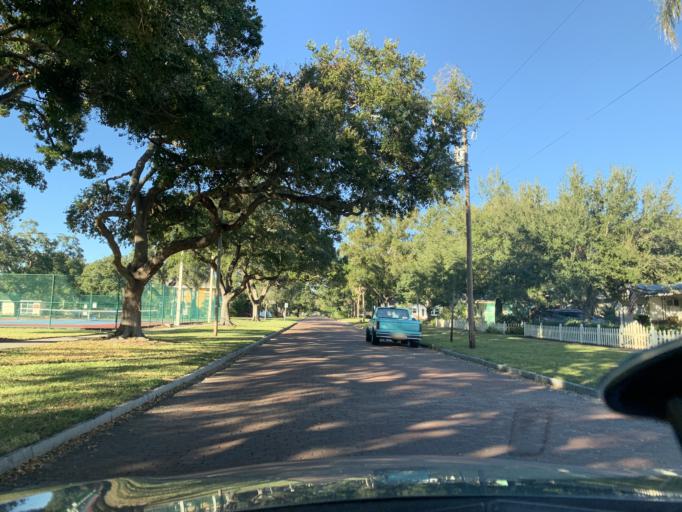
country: US
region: Florida
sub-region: Pinellas County
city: Gulfport
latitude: 27.7427
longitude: -82.7052
